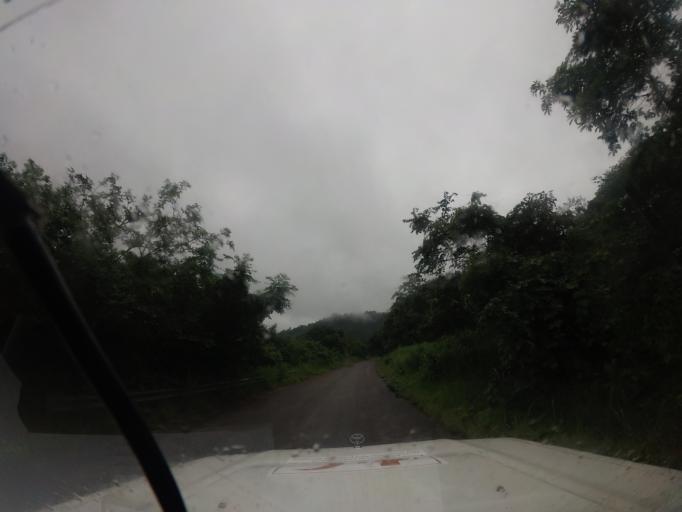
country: SL
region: Northern Province
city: Kabala
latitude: 9.4557
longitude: -11.6863
